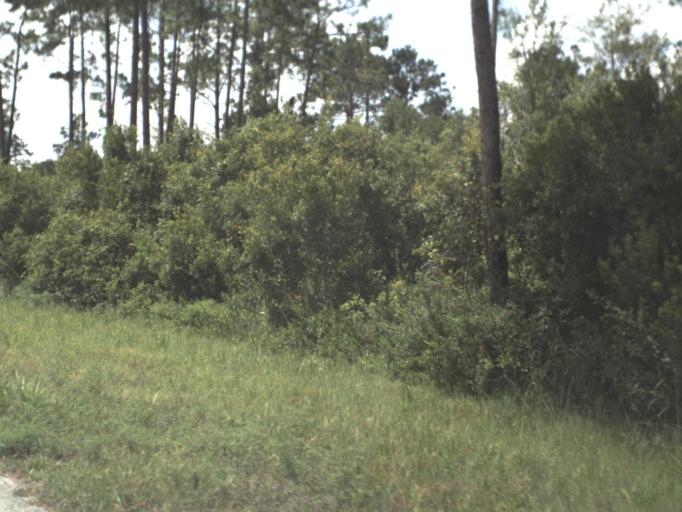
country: US
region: Florida
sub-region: Baker County
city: Macclenny
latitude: 30.5244
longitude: -82.2961
